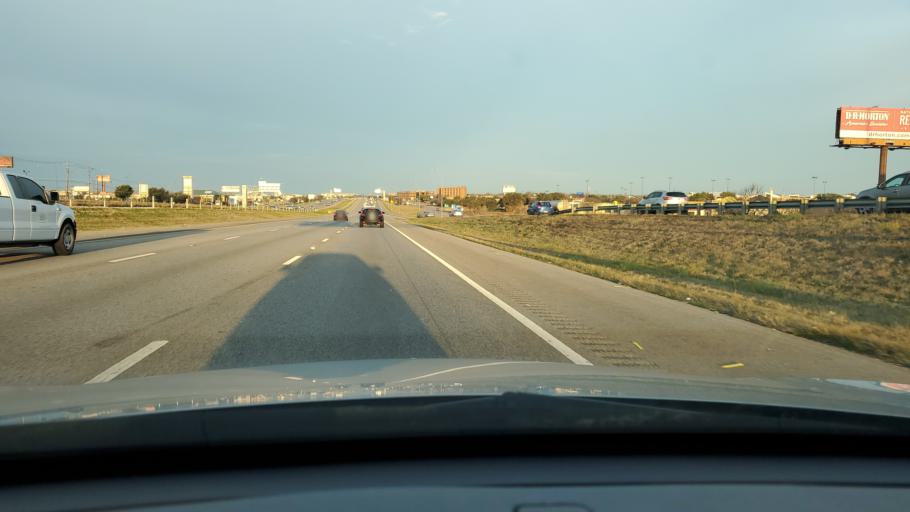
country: US
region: Texas
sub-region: Bell County
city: Killeen
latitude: 31.0878
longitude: -97.7132
